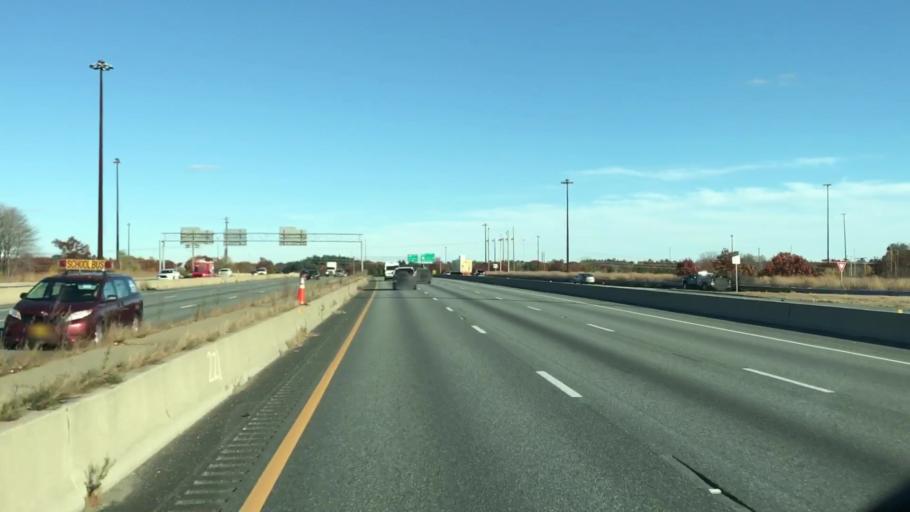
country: US
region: Massachusetts
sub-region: Middlesex County
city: Lowell
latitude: 42.6071
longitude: -71.3287
